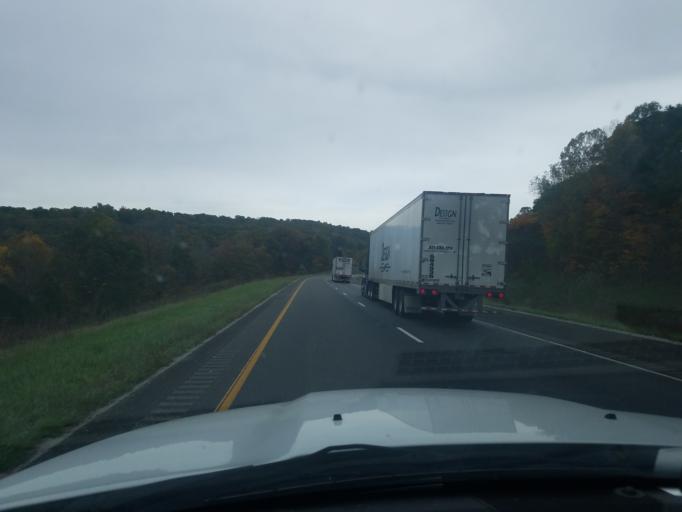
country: US
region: Indiana
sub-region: Crawford County
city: English
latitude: 38.2433
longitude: -86.4152
